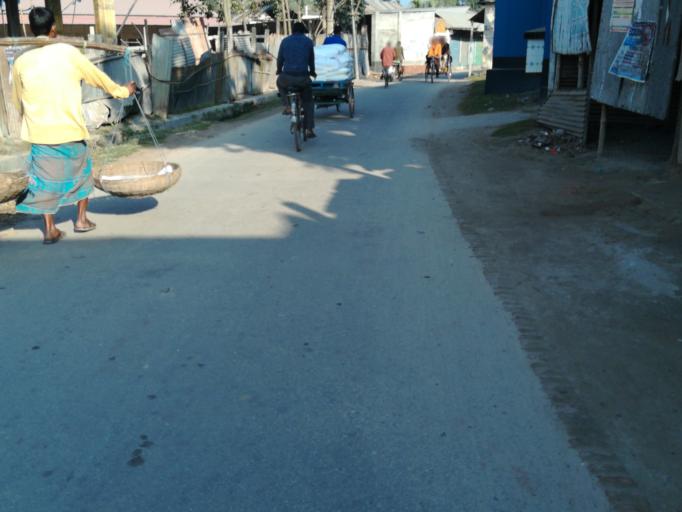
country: BD
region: Rangpur Division
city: Nageswari
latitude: 25.8121
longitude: 89.6481
